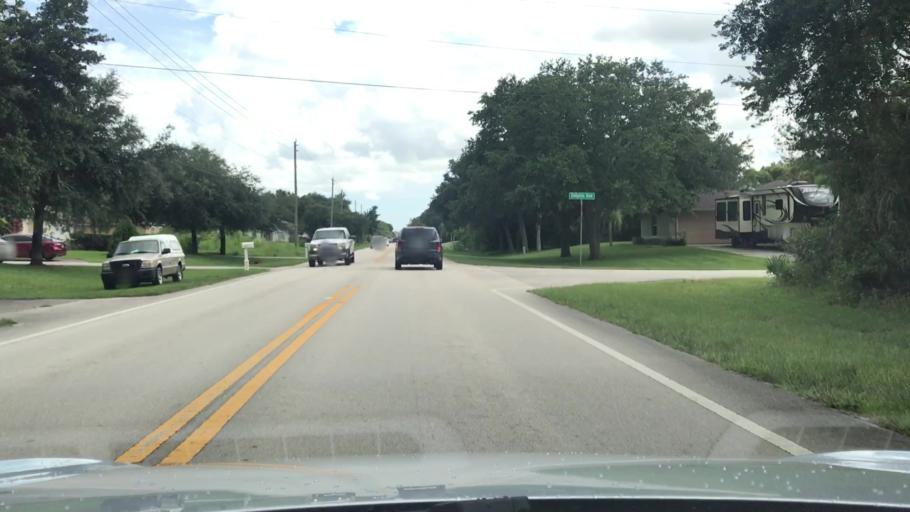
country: US
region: Florida
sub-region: Indian River County
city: Sebastian
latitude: 27.7857
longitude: -80.4982
